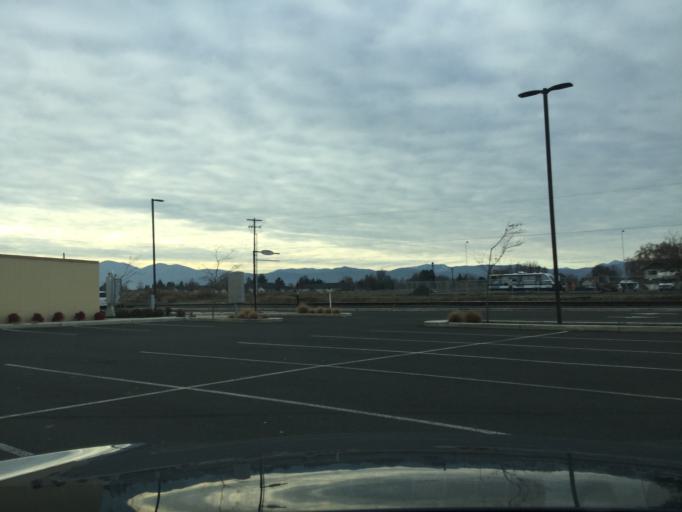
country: US
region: Oregon
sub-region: Jackson County
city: Central Point
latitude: 42.3717
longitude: -122.9161
